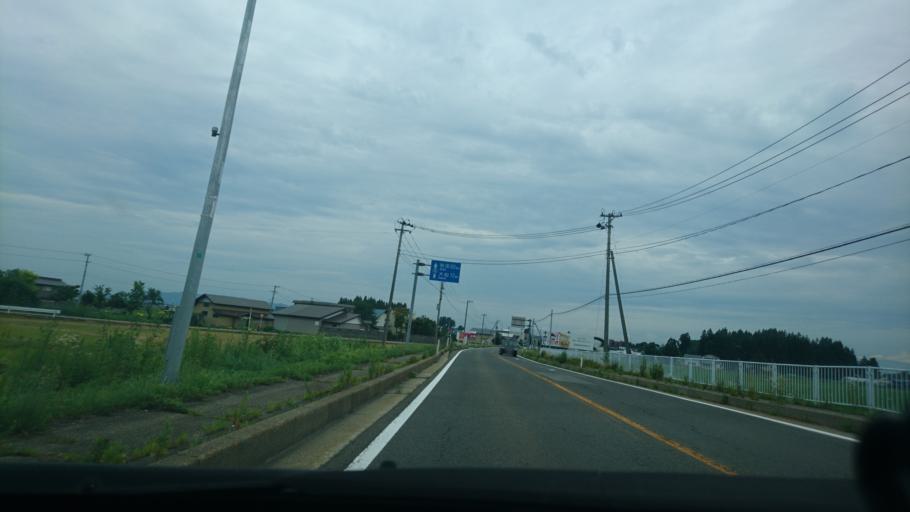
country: JP
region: Akita
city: Yokotemachi
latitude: 39.3925
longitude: 140.5676
